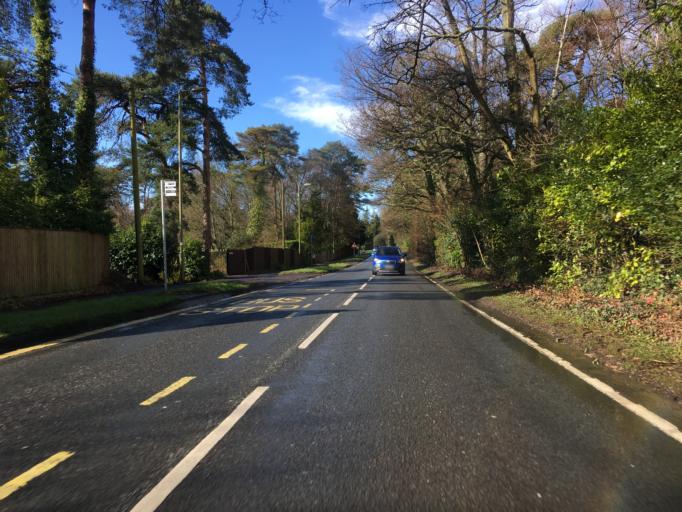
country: GB
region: England
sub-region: Southampton
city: Southampton
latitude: 50.9610
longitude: -1.4070
